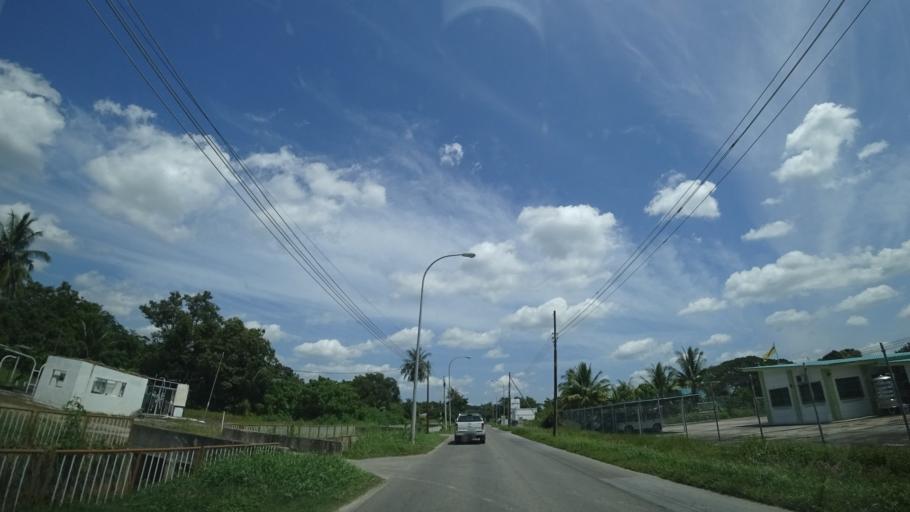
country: BN
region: Brunei and Muara
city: Bandar Seri Begawan
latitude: 4.8691
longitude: 114.8517
